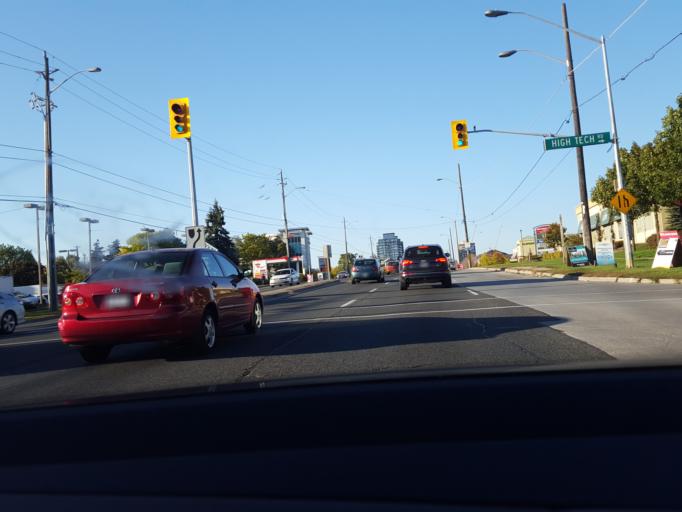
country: CA
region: Ontario
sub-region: York
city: Richmond Hill
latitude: 43.8415
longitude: -79.4301
